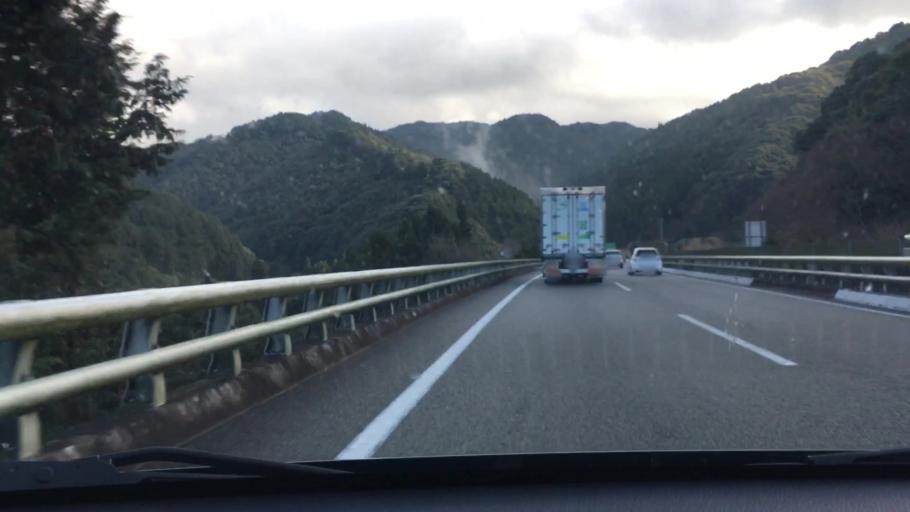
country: JP
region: Kumamoto
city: Hitoyoshi
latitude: 32.1375
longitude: 130.8026
